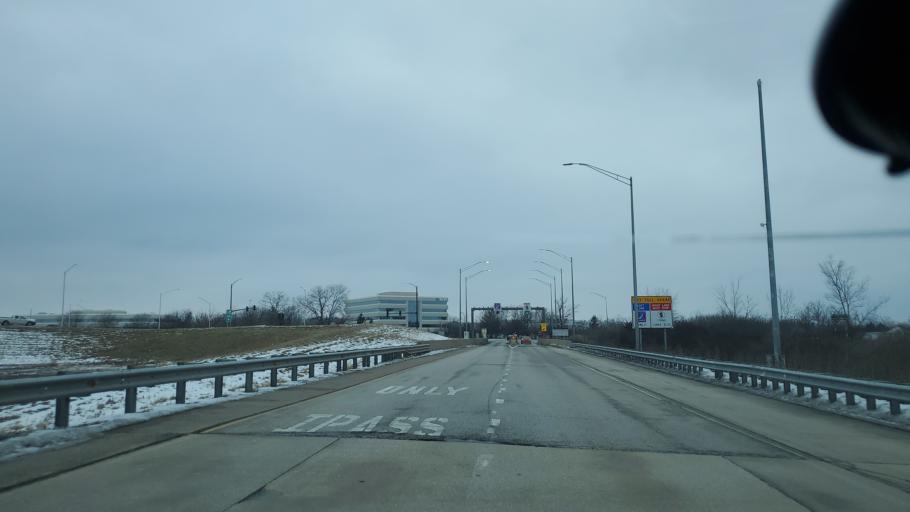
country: US
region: Illinois
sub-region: Kane County
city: North Aurora
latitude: 41.7993
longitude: -88.2801
